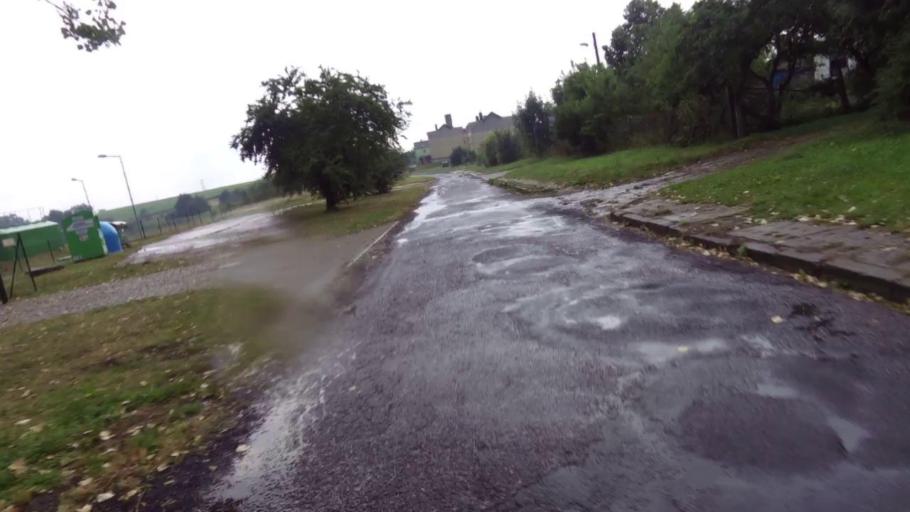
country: PL
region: West Pomeranian Voivodeship
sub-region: Powiat choszczenski
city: Recz
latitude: 53.2707
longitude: 15.4600
